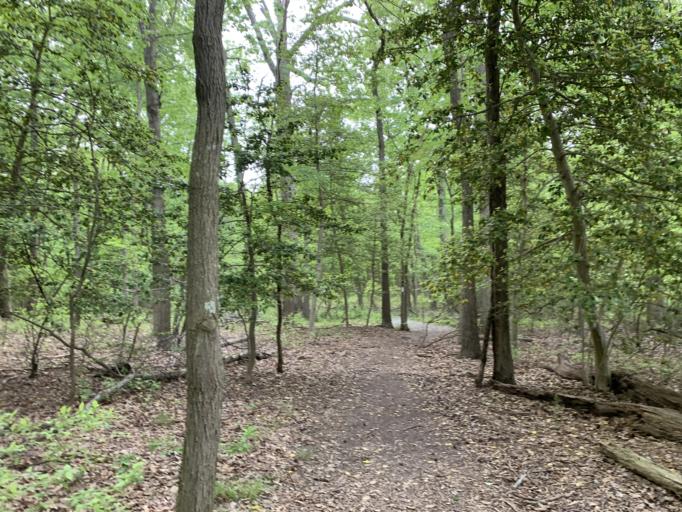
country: US
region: Maryland
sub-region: Baltimore County
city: Bowleys Quarters
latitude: 39.3451
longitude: -76.3712
